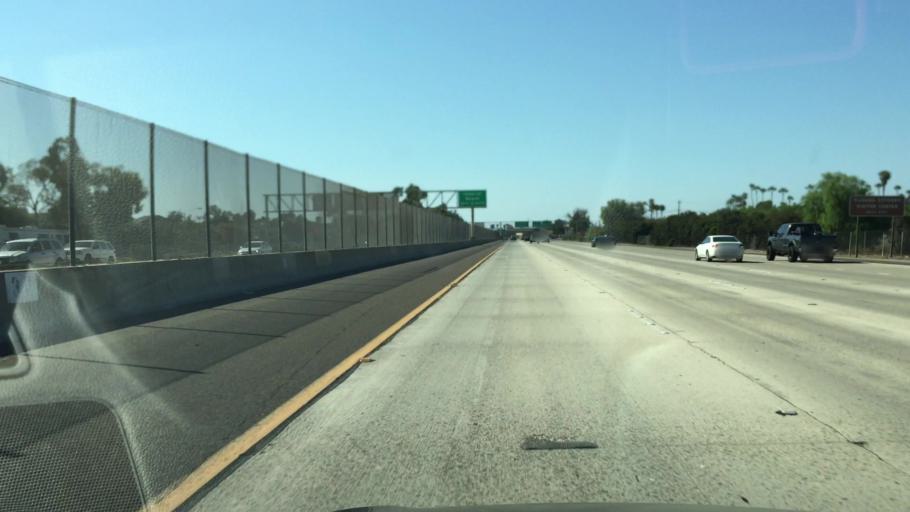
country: US
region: California
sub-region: San Diego County
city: Imperial Beach
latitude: 32.5700
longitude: -117.0773
